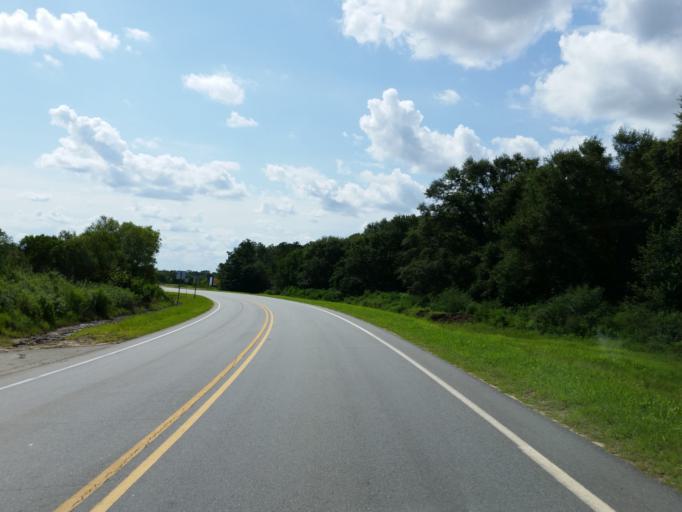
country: US
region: Georgia
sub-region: Turner County
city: Ashburn
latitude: 31.6649
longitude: -83.6038
